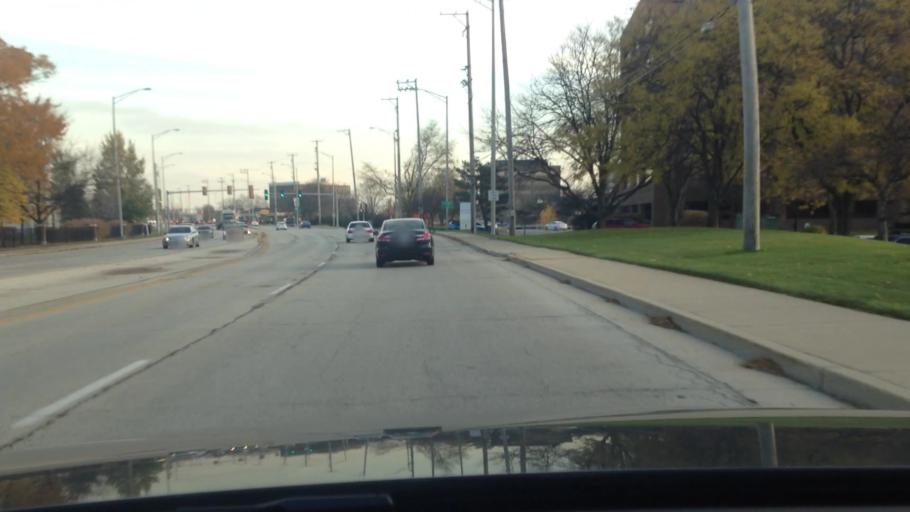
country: US
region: Illinois
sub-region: Cook County
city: Arlington Heights
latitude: 42.0462
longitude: -87.9875
